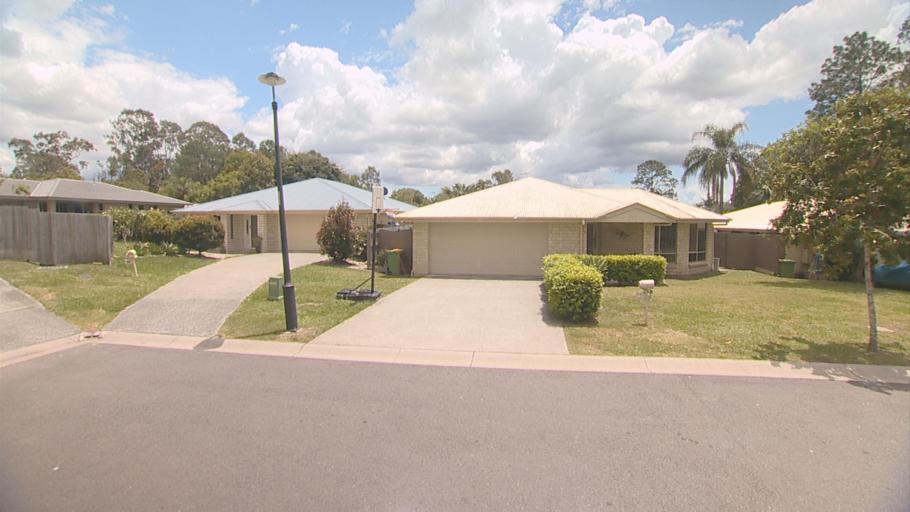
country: AU
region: Queensland
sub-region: Logan
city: Waterford West
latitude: -27.6854
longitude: 153.1260
